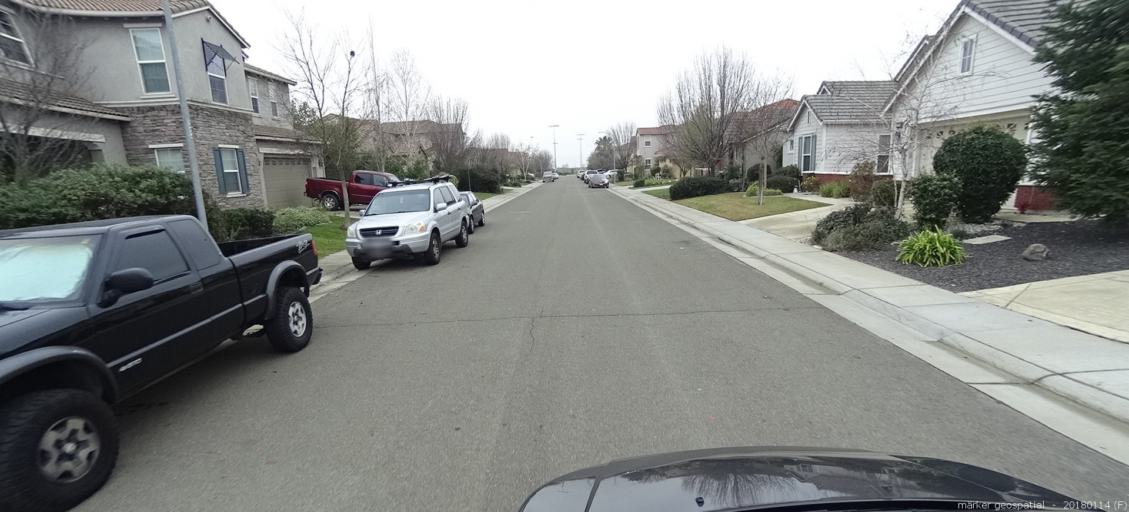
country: US
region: California
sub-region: Sacramento County
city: Rancho Cordova
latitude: 38.5379
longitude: -121.2361
